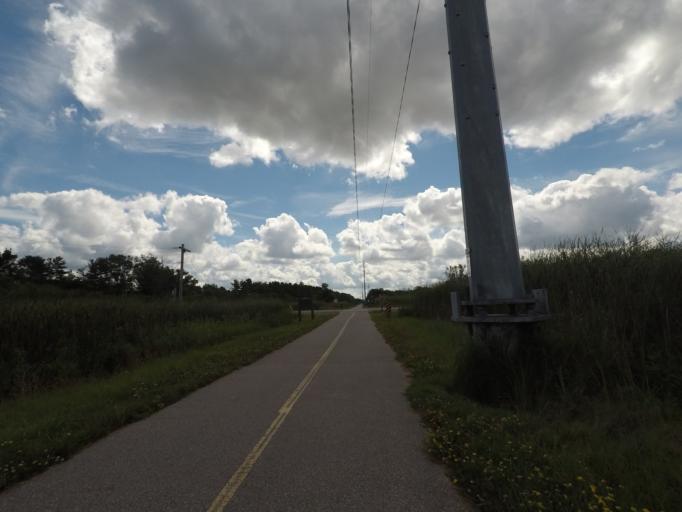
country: US
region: Wisconsin
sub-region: Waukesha County
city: Pewaukee
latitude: 43.0542
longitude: -88.2854
